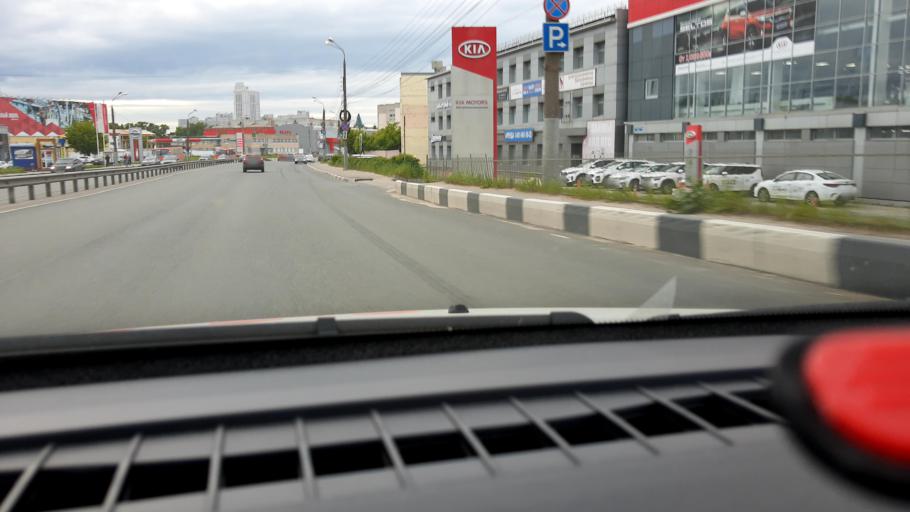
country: RU
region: Nizjnij Novgorod
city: Nizhniy Novgorod
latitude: 56.3105
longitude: 43.9038
